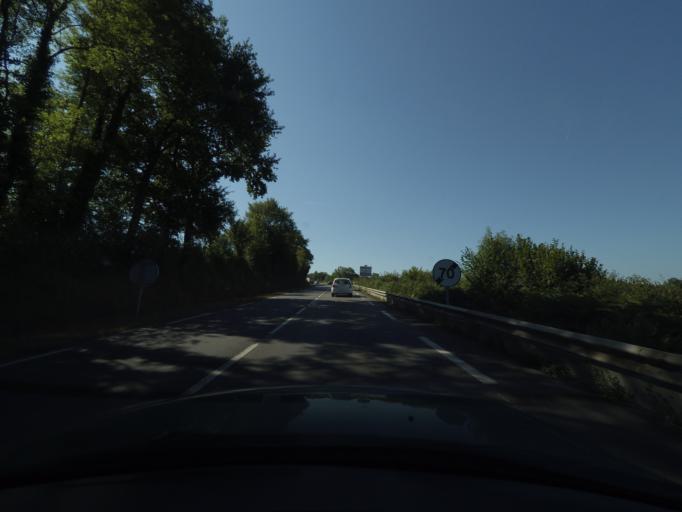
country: FR
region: Limousin
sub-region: Departement de la Haute-Vienne
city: Peyrat-de-Bellac
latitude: 46.1621
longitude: 0.9597
